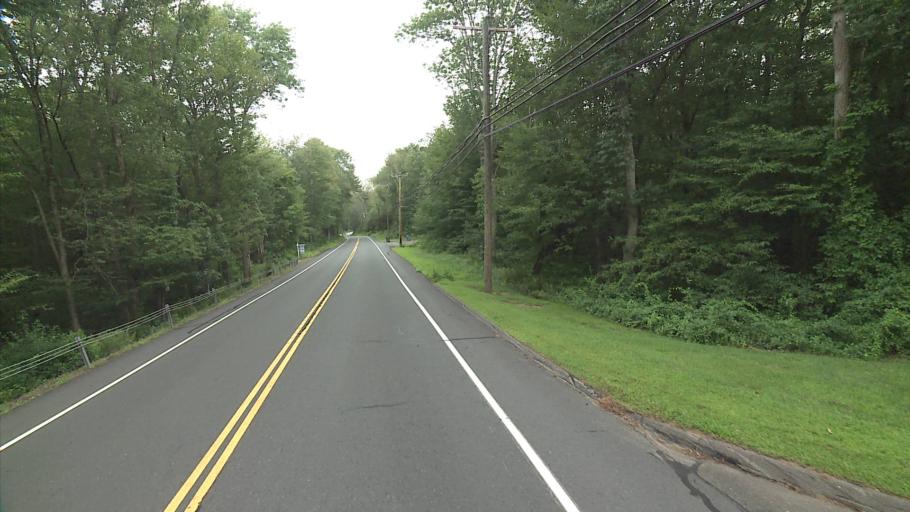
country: US
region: Connecticut
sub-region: Tolland County
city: Tolland
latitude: 41.8864
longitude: -72.3223
